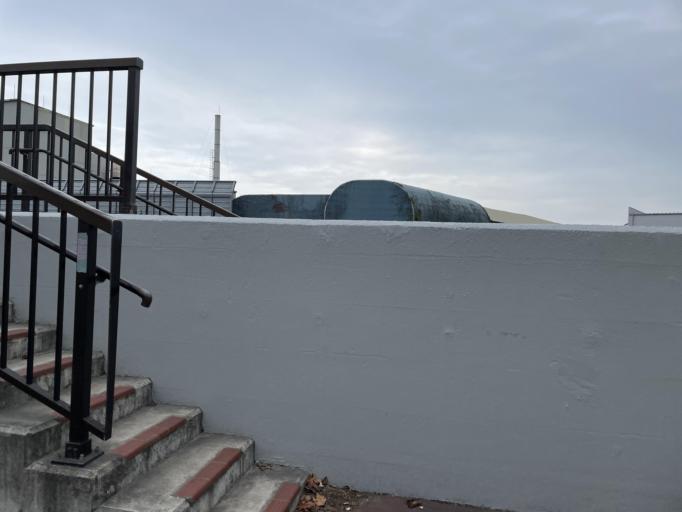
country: JP
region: Tokyo
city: Urayasu
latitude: 35.6650
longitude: 139.8816
